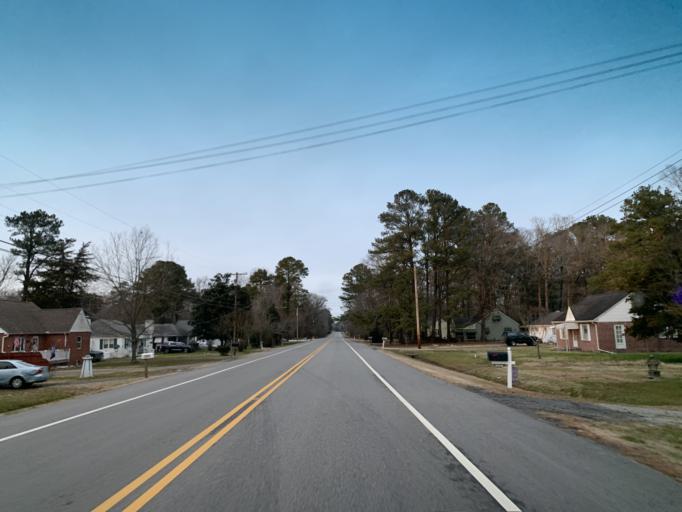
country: US
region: Maryland
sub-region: Worcester County
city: Pocomoke City
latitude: 38.0689
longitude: -75.5472
